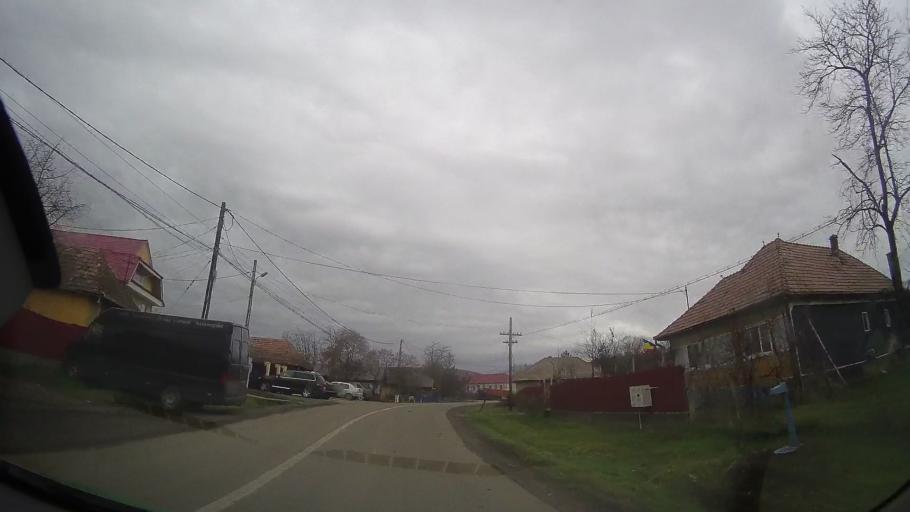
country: RO
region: Mures
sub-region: Comuna Craesti
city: Craiesti
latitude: 46.7577
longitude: 24.4251
